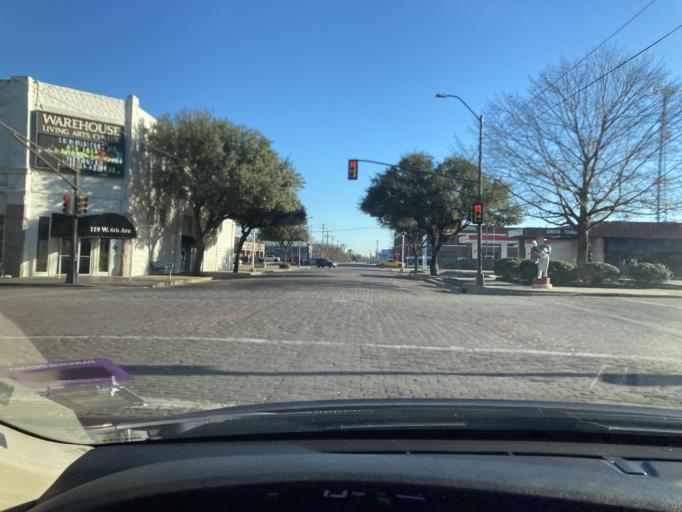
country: US
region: Texas
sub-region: Navarro County
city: Corsicana
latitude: 32.0923
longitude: -96.4644
